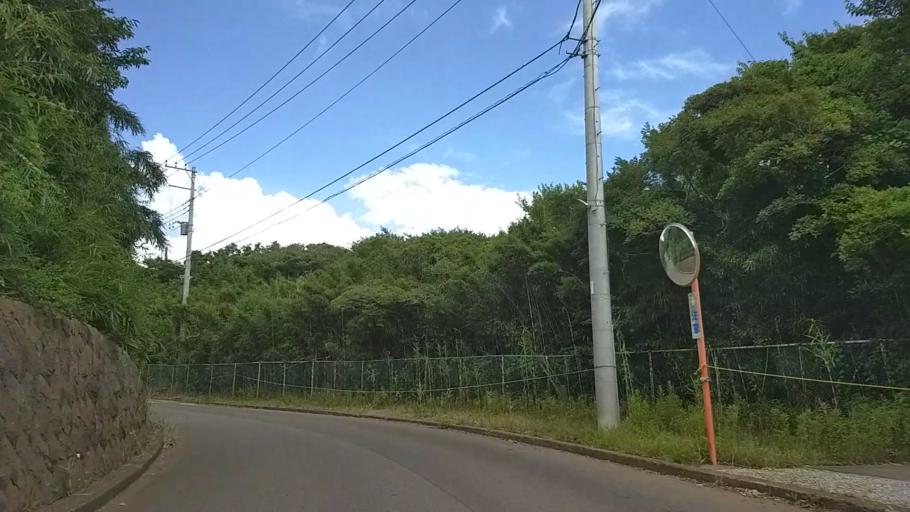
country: JP
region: Kanagawa
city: Miura
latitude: 35.1929
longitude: 139.6205
